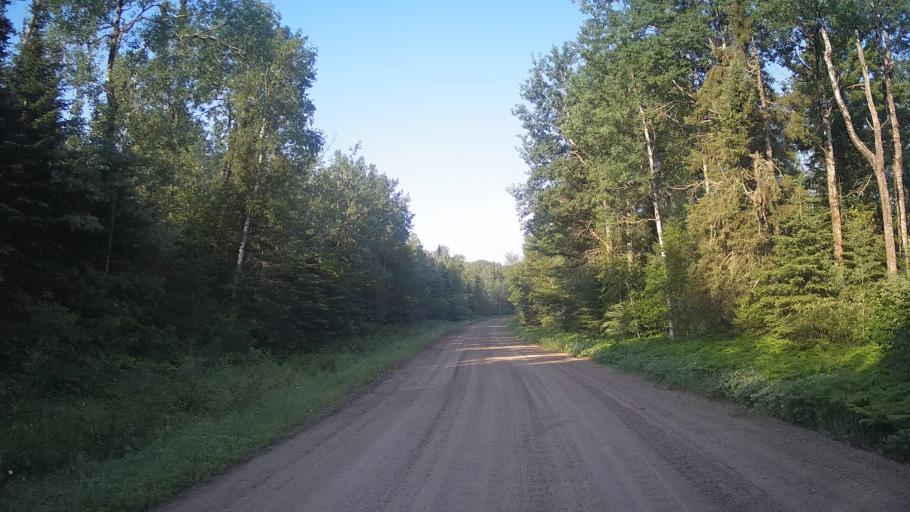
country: CA
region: Ontario
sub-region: Rainy River District
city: Atikokan
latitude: 49.4006
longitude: -91.6611
